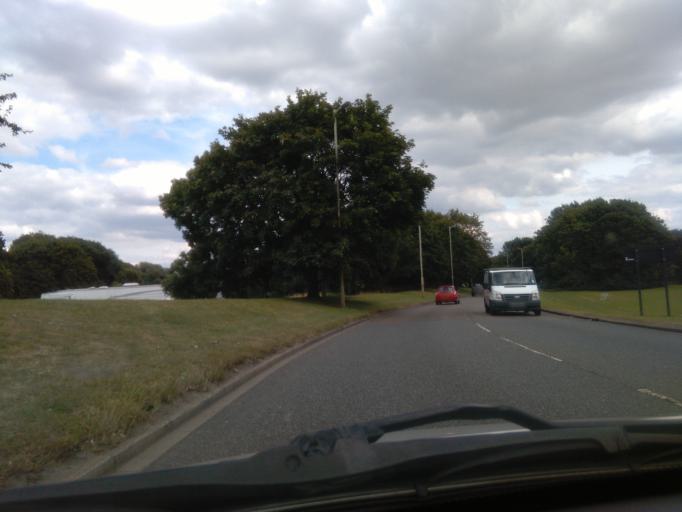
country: GB
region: England
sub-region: Bedford
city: Bedford
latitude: 52.1317
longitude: -0.4569
